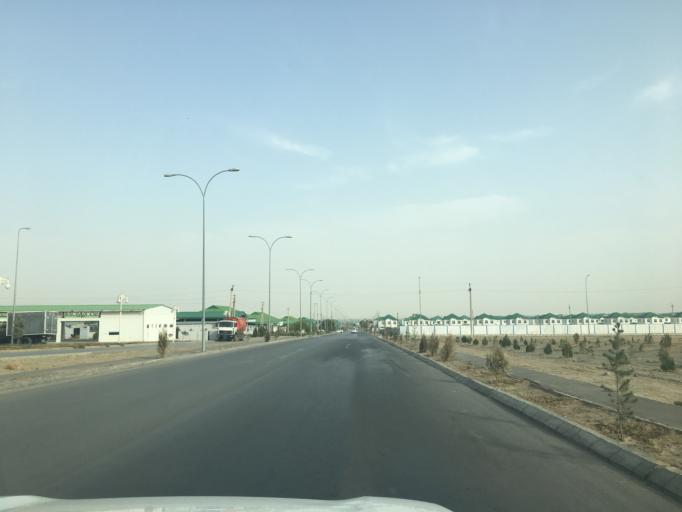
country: TM
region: Ahal
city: Annau
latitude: 37.8874
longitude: 58.4813
